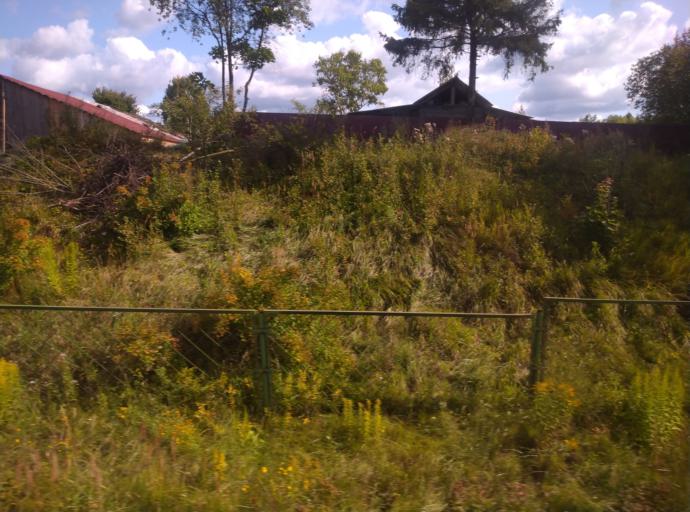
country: RU
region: Leningrad
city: Krasnyy Bor
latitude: 59.6840
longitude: 30.6962
